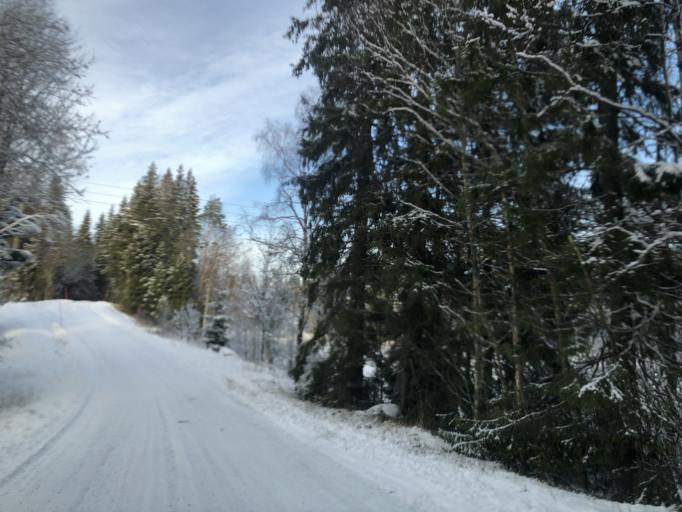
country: SE
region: Vaestra Goetaland
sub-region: Ulricehamns Kommun
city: Ulricehamn
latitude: 57.7736
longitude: 13.5234
